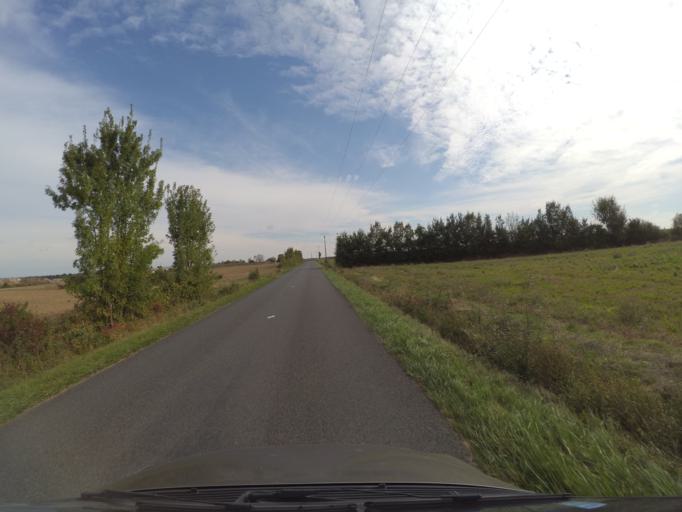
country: FR
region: Pays de la Loire
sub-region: Departement de Maine-et-Loire
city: Saint-Jean
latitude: 47.1916
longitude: -0.3441
